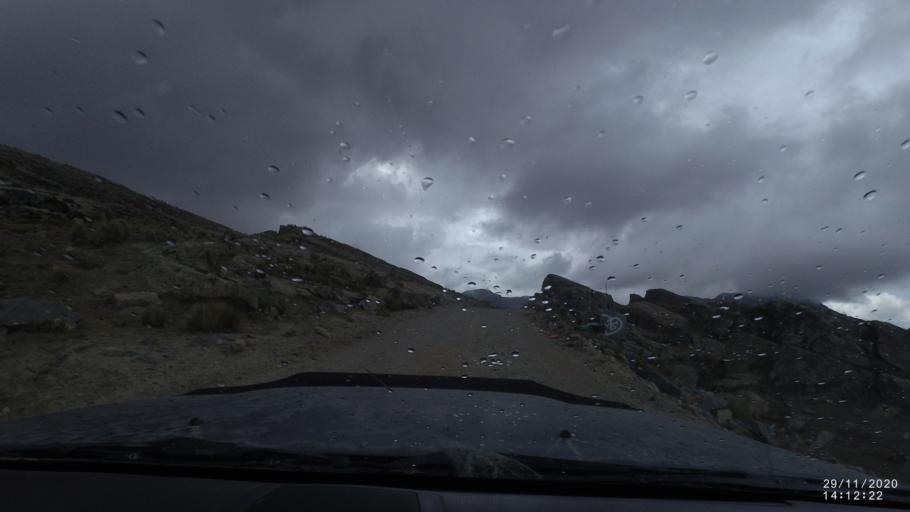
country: BO
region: Cochabamba
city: Sipe Sipe
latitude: -17.2386
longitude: -66.3928
